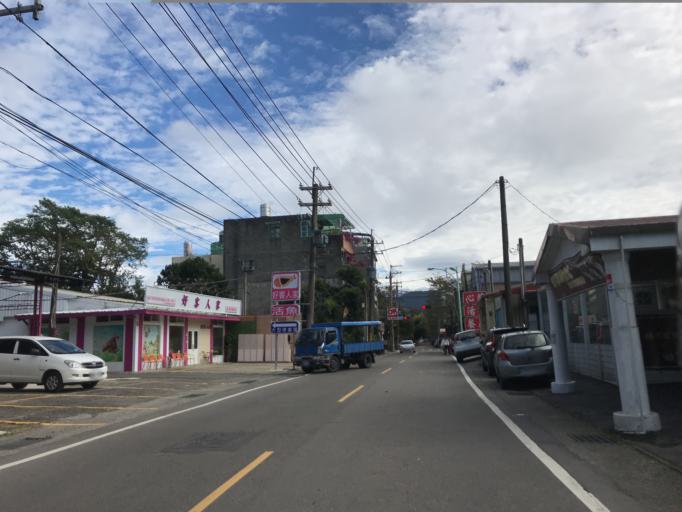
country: TW
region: Taiwan
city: Daxi
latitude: 24.8432
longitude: 121.2402
